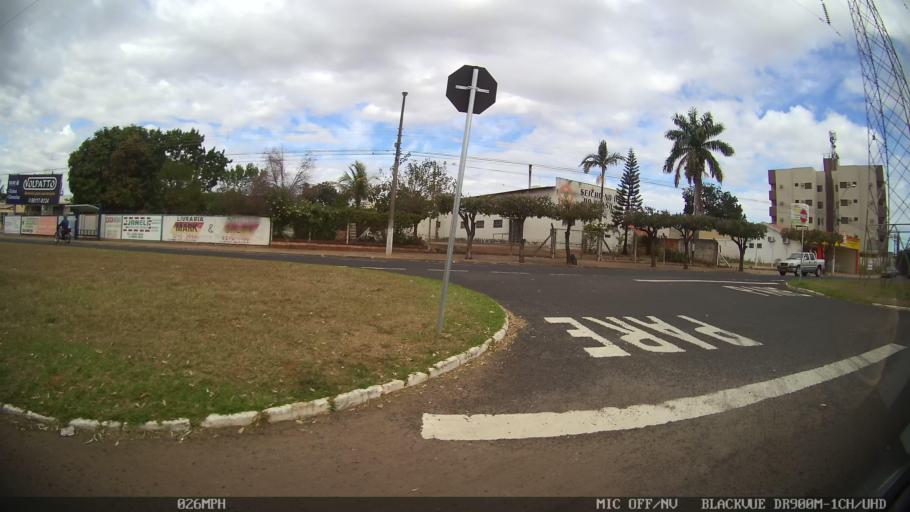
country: BR
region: Sao Paulo
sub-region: Bady Bassitt
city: Bady Bassitt
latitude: -20.8135
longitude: -49.4999
